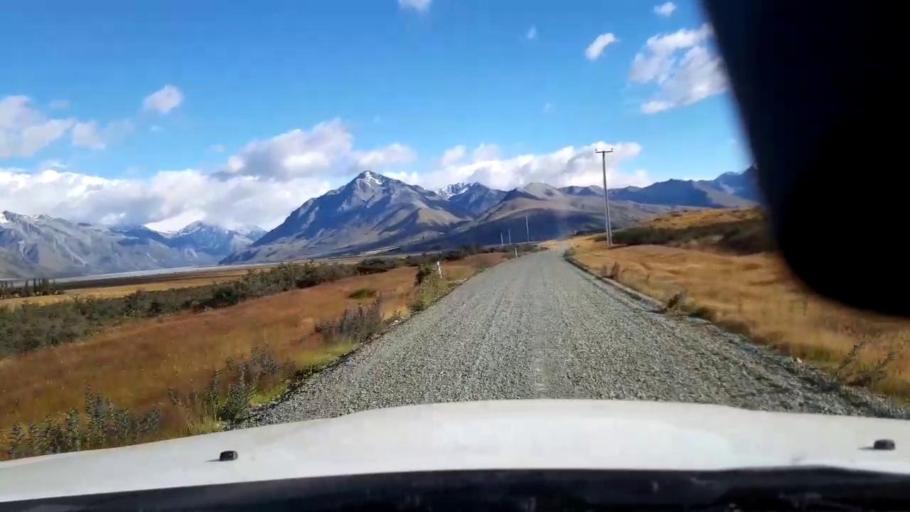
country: NZ
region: Canterbury
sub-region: Timaru District
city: Pleasant Point
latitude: -43.7605
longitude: 170.5697
